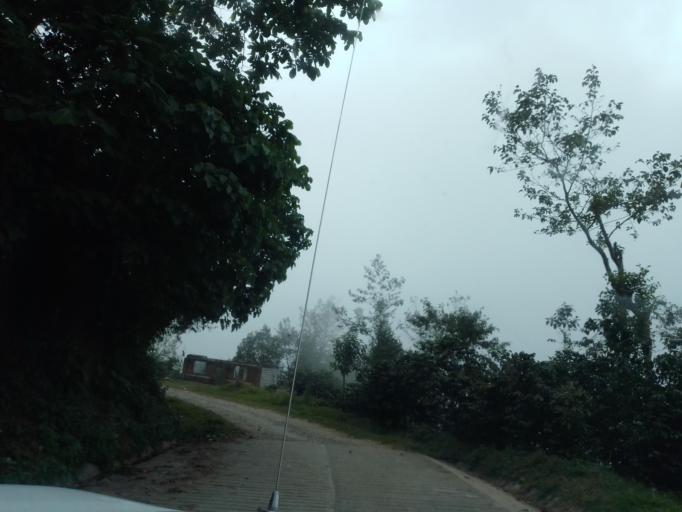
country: MX
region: Chiapas
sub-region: Union Juarez
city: Santo Domingo
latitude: 15.0870
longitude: -92.0885
